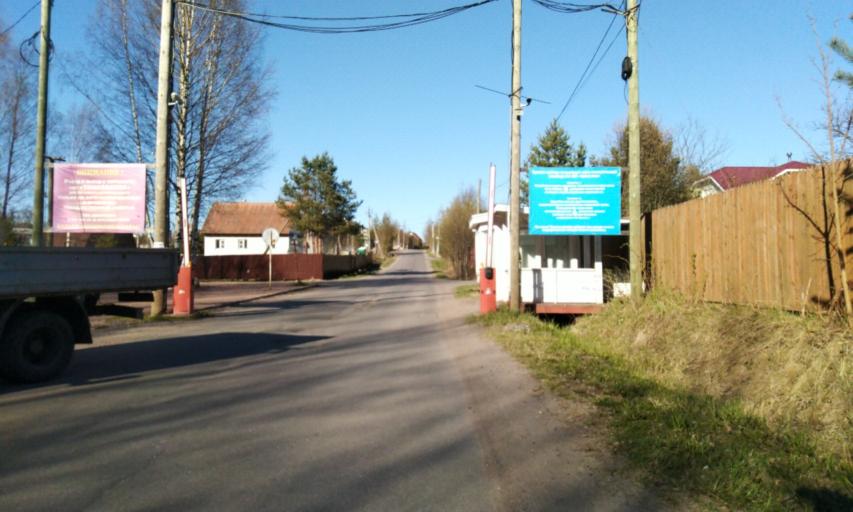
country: RU
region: Leningrad
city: Toksovo
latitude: 60.1435
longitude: 30.5562
